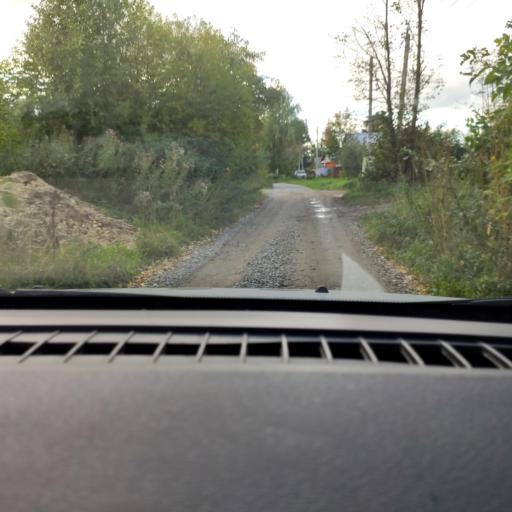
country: RU
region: Perm
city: Perm
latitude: 58.0982
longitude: 56.3732
